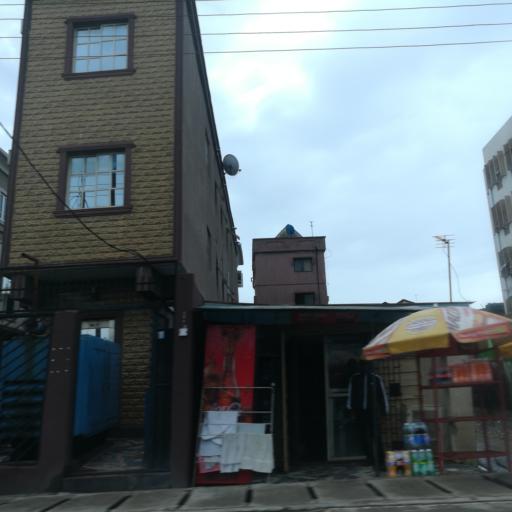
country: NG
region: Lagos
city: Makoko
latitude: 6.4923
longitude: 3.3788
